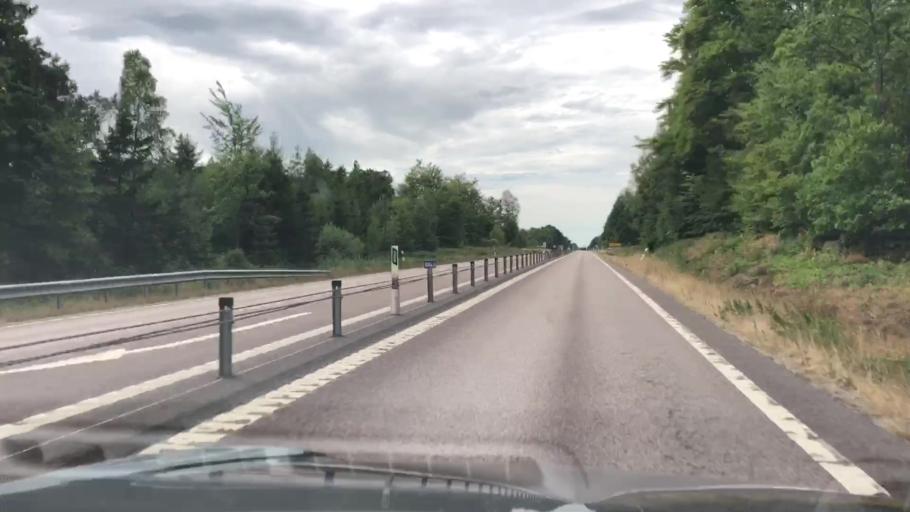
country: SE
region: Kalmar
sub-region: Torsas Kommun
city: Torsas
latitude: 56.2767
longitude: 15.9713
